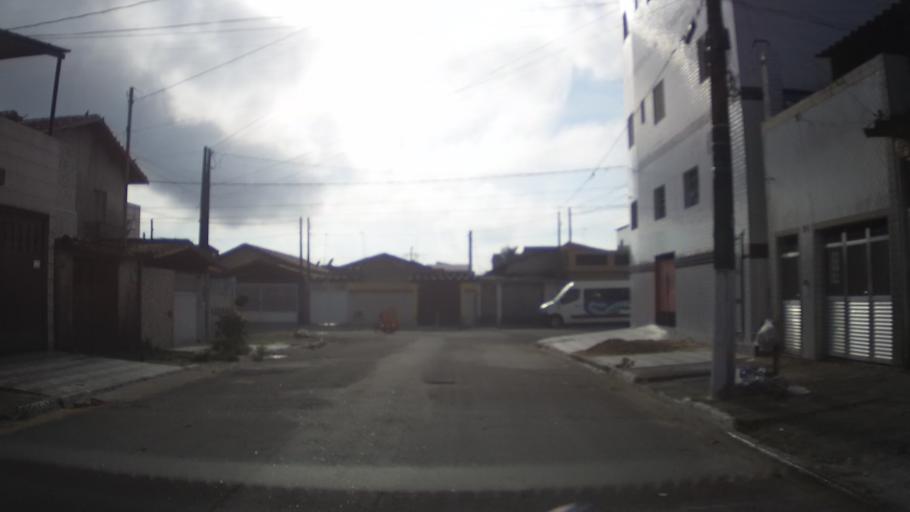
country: BR
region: Sao Paulo
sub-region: Praia Grande
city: Praia Grande
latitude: -24.0129
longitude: -46.4789
